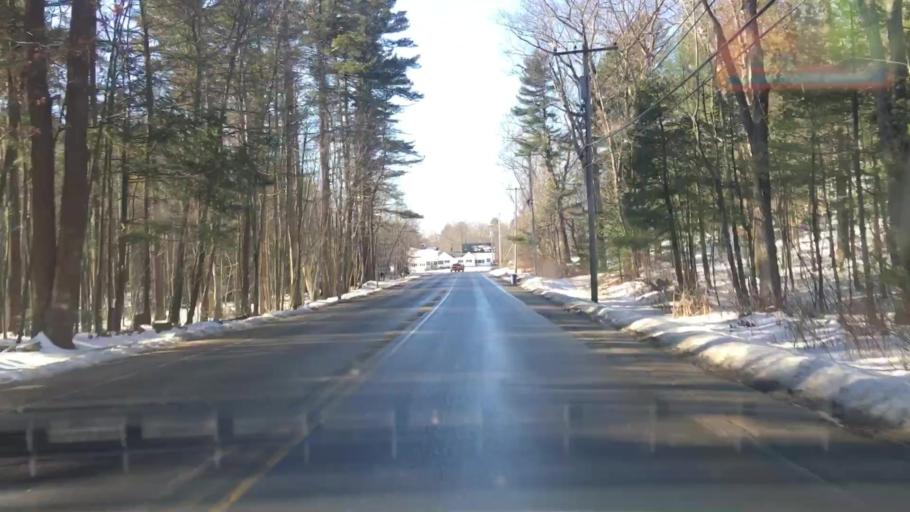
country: US
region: Maine
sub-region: Cumberland County
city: Falmouth
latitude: 43.7226
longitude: -70.2595
